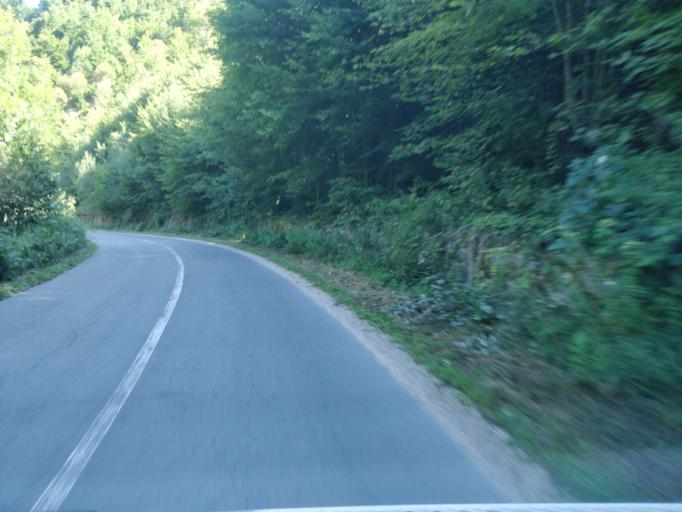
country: RO
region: Cluj
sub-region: Comuna Sacueu
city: Sacuieu
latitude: 46.8397
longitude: 22.8626
